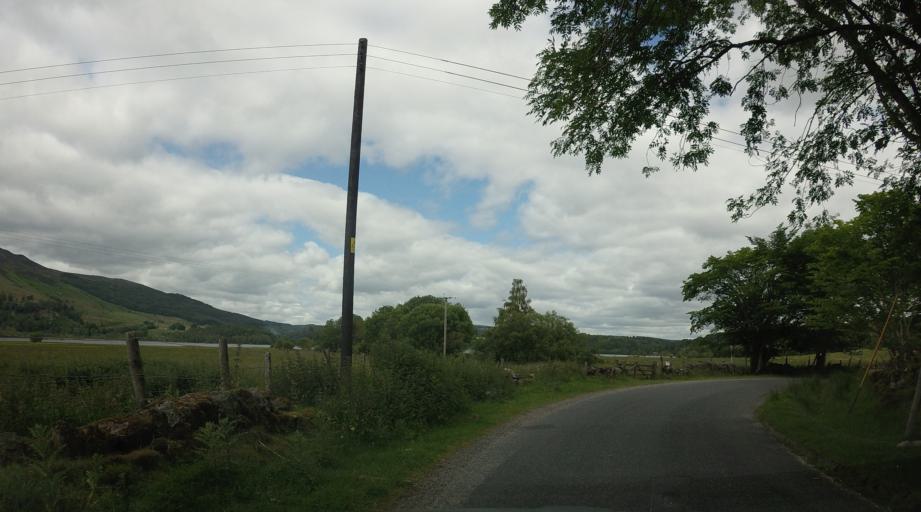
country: GB
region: Scotland
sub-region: Perth and Kinross
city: Aberfeldy
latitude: 56.6932
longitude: -4.1319
